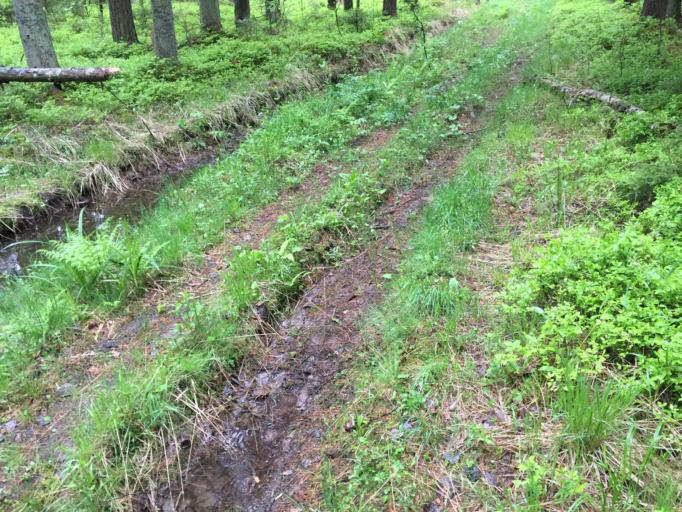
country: LV
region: Ogre
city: Jumprava
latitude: 56.6770
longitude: 24.9281
